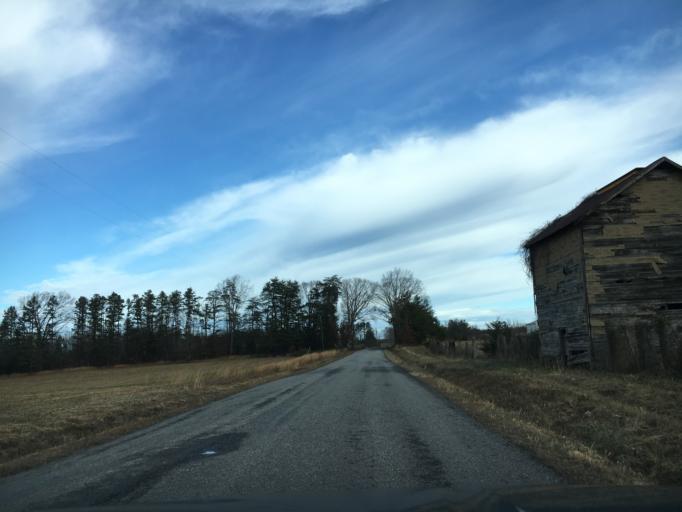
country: US
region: Virginia
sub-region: Nottoway County
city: Crewe
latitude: 37.2449
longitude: -78.2262
